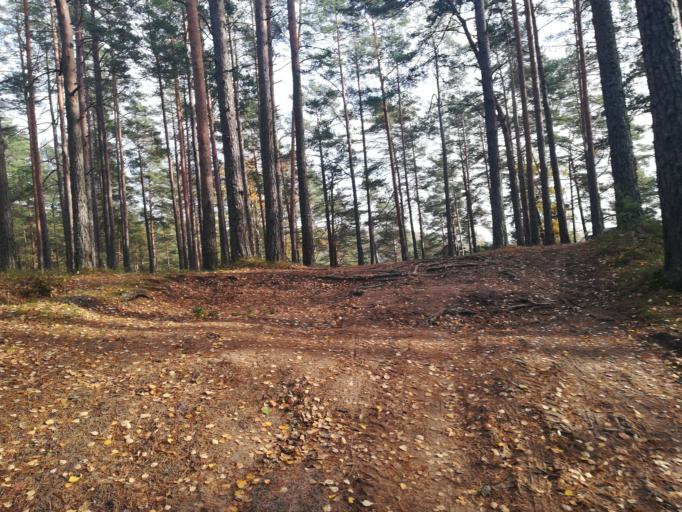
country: RU
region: Leningrad
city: Ust'-Luga
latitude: 59.7513
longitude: 28.1518
